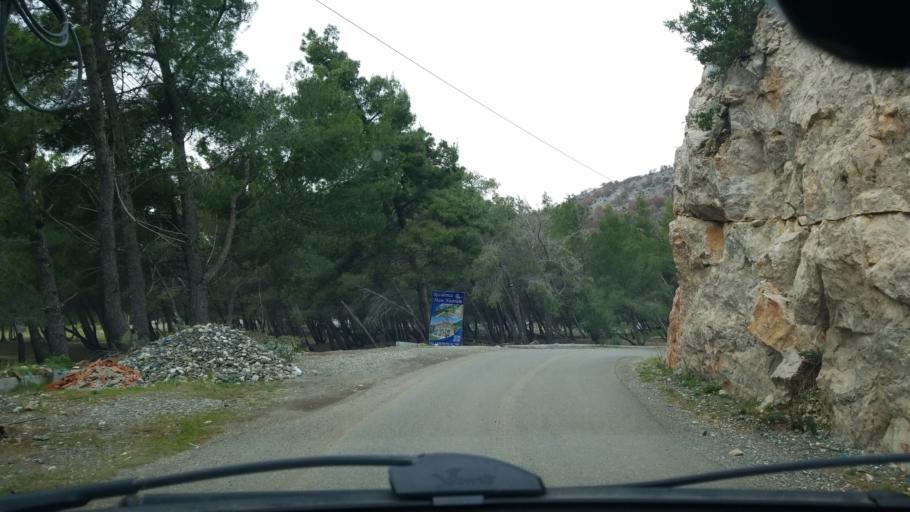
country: AL
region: Lezhe
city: Shengjin
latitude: 41.8213
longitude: 19.5620
